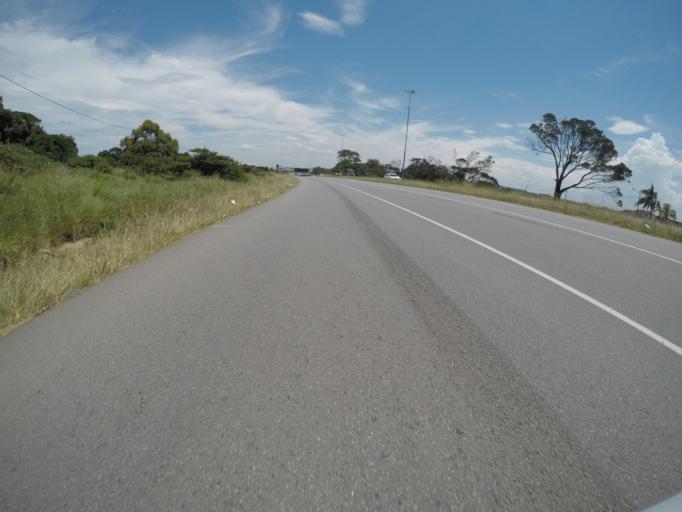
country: ZA
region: Eastern Cape
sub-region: Buffalo City Metropolitan Municipality
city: East London
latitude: -33.0351
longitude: 27.8426
